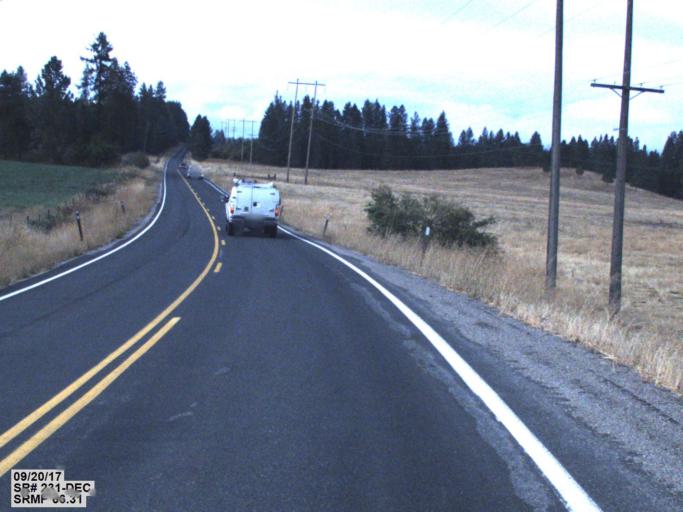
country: US
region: Washington
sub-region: Stevens County
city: Chewelah
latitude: 48.1044
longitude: -117.7578
